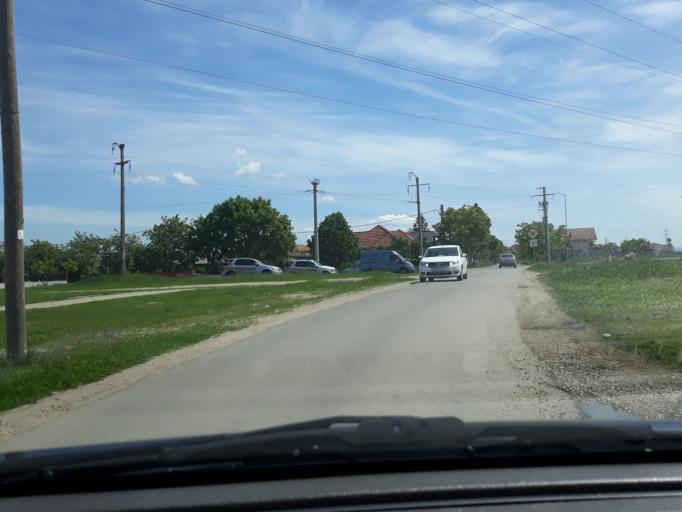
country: RO
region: Bihor
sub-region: Comuna Santandrei
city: Santandrei
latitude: 47.0694
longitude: 21.8587
